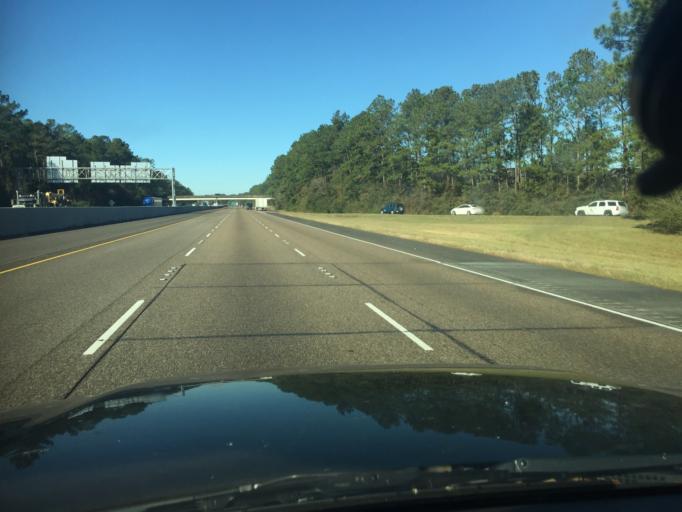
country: US
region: Louisiana
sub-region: Saint Tammany Parish
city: Slidell
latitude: 30.3075
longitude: -89.7453
